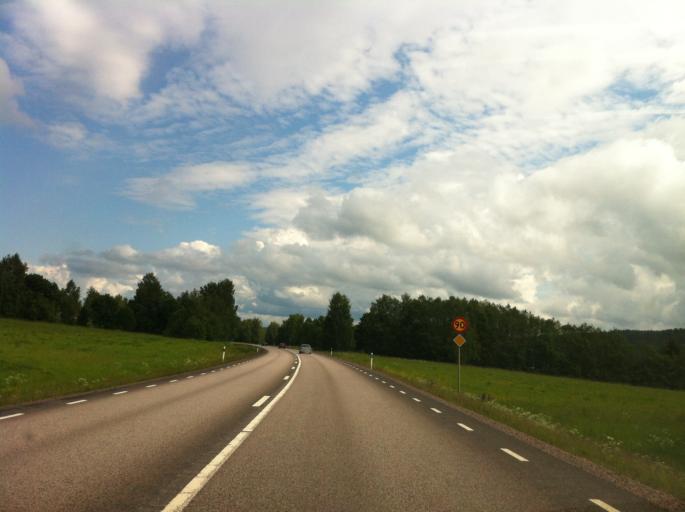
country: SE
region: Vaermland
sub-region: Sunne Kommun
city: Sunne
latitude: 59.8709
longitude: 13.1386
